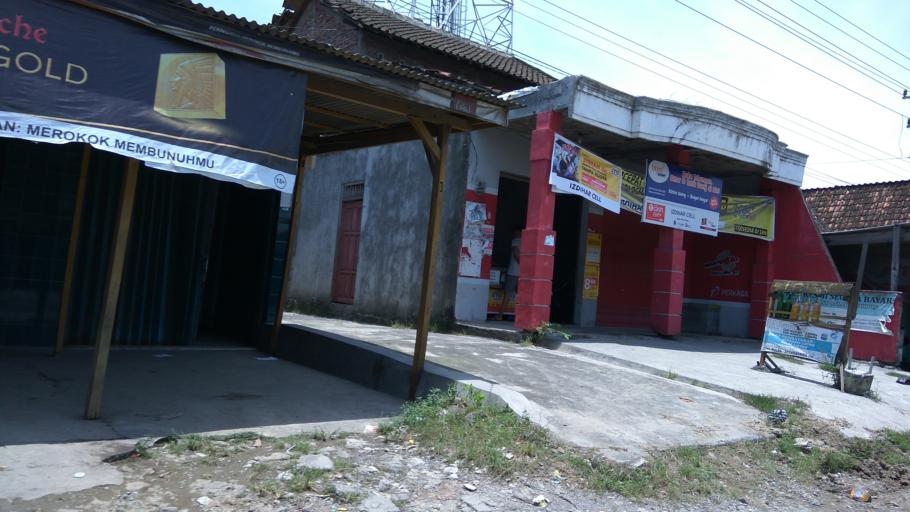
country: ID
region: Central Java
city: Mranggen
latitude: -7.0324
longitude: 110.5421
